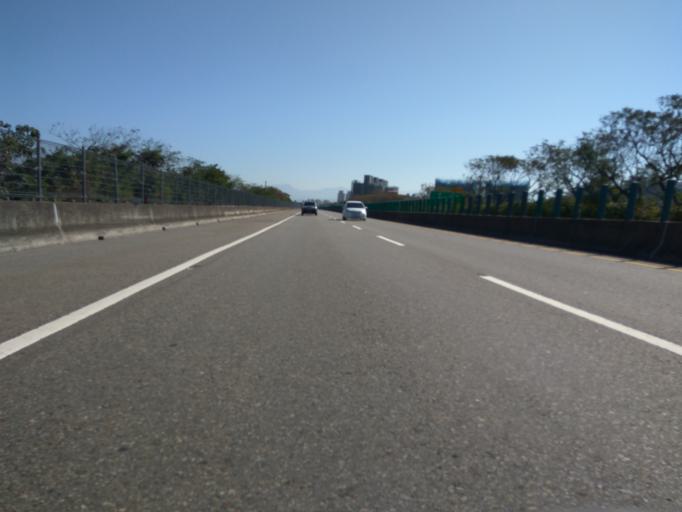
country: TW
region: Taiwan
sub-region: Hsinchu
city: Hsinchu
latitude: 24.8292
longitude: 120.9618
